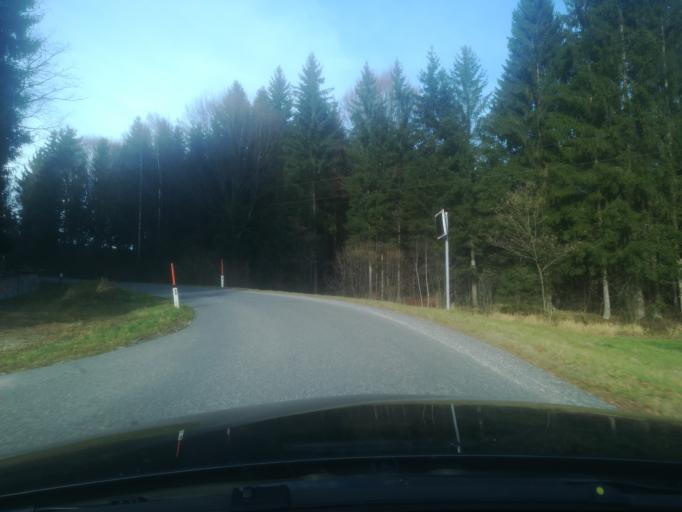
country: AT
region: Upper Austria
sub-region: Politischer Bezirk Perg
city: Perg
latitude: 48.3228
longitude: 14.6596
